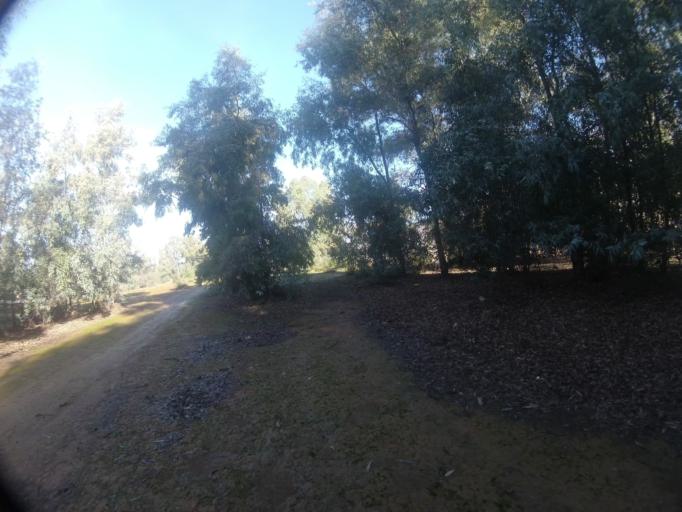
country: ES
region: Andalusia
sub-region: Provincia de Huelva
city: Gibraleon
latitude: 37.3738
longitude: -6.9757
